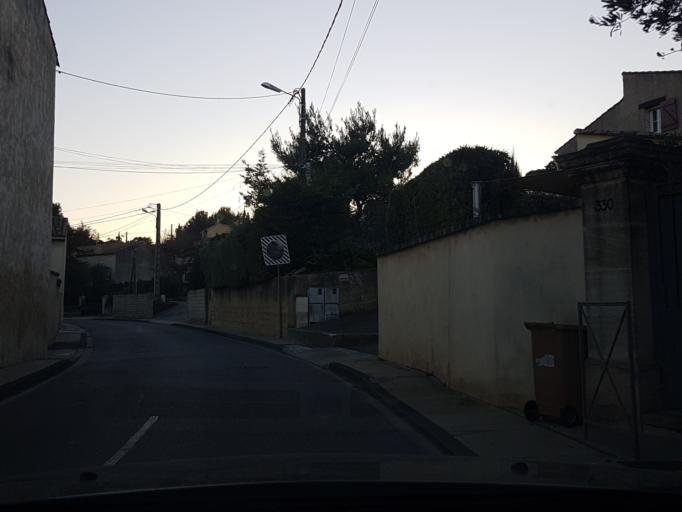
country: FR
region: Provence-Alpes-Cote d'Azur
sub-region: Departement du Vaucluse
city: Vedene
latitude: 43.9732
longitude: 4.9000
